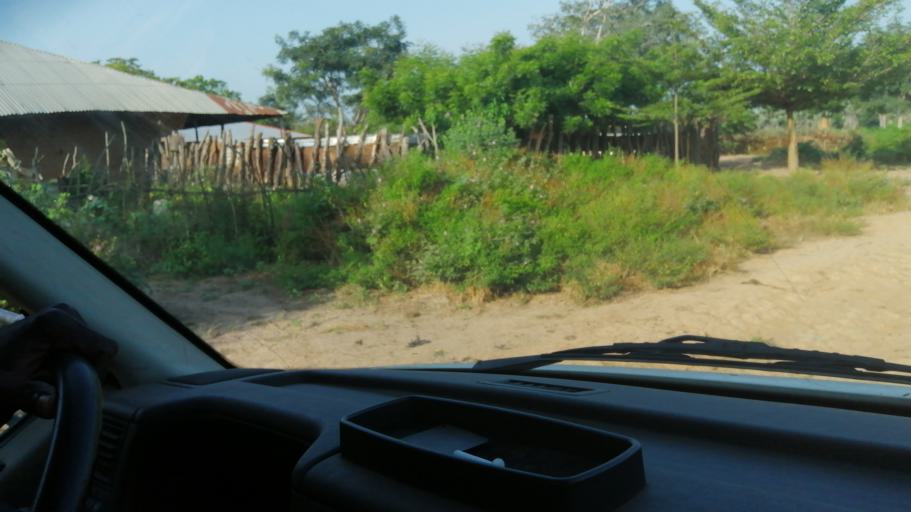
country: GW
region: Oio
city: Mansoa
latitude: 11.9997
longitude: -15.4699
